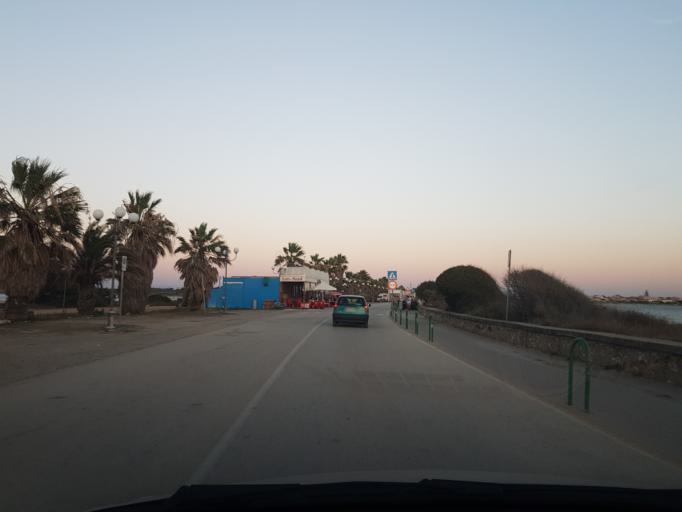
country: IT
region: Sardinia
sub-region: Provincia di Oristano
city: Riola Sardo
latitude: 40.0329
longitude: 8.4016
